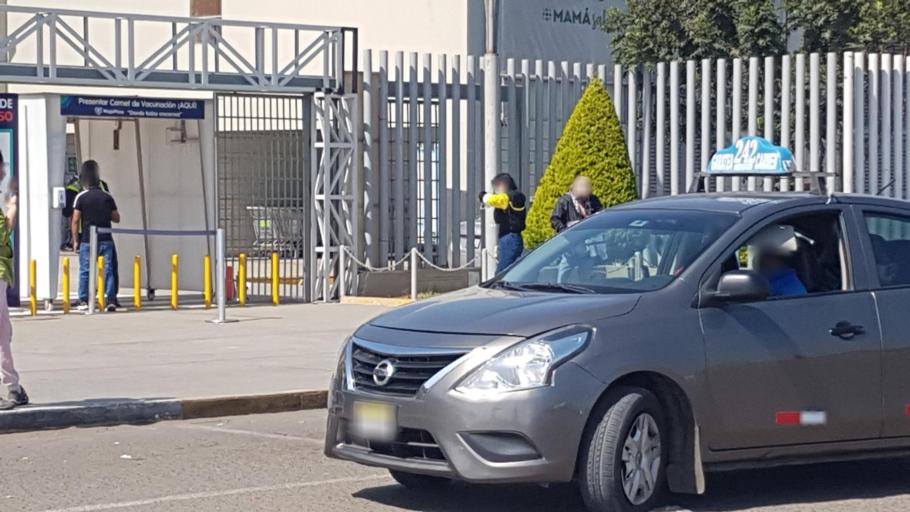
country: PE
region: Ancash
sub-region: Provincia de Santa
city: Chimbote
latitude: -9.1033
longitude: -78.5581
